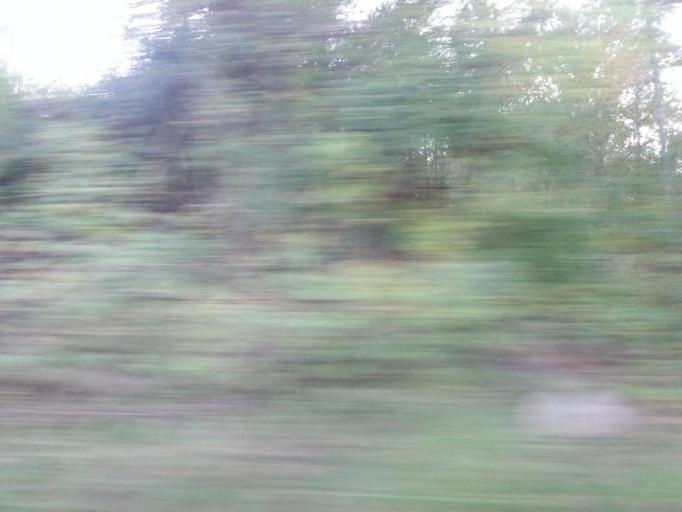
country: US
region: Tennessee
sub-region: Sevier County
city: Seymour
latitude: 35.7860
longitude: -83.7395
